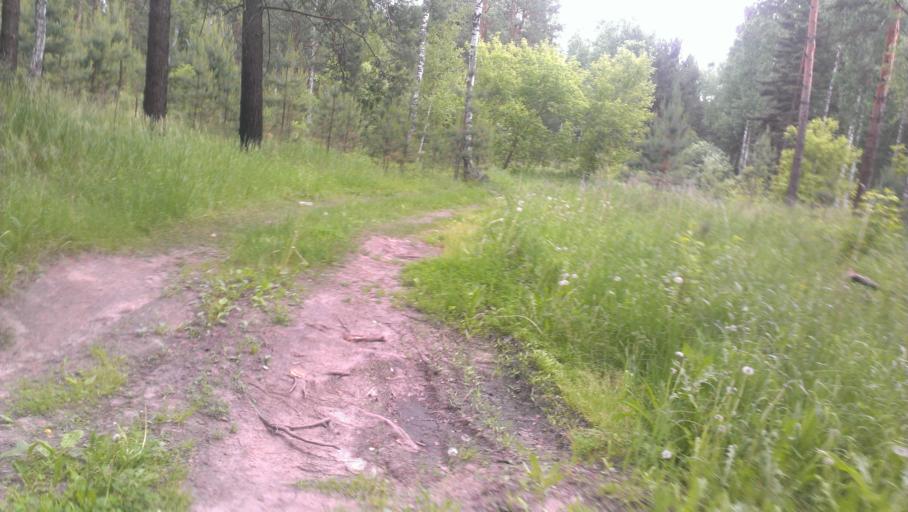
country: RU
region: Altai Krai
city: Sannikovo
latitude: 53.3445
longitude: 84.0434
